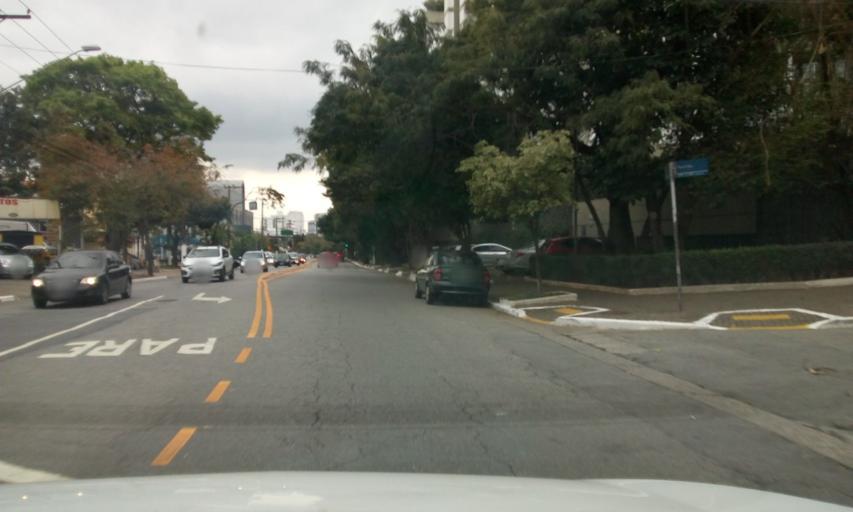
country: BR
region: Sao Paulo
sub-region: Sao Paulo
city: Sao Paulo
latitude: -23.6138
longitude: -46.6440
